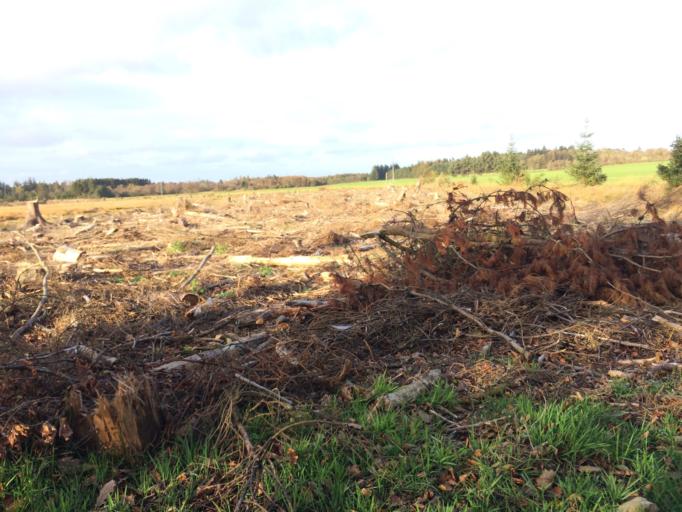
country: DK
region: Central Jutland
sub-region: Holstebro Kommune
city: Ulfborg
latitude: 56.2103
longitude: 8.4731
